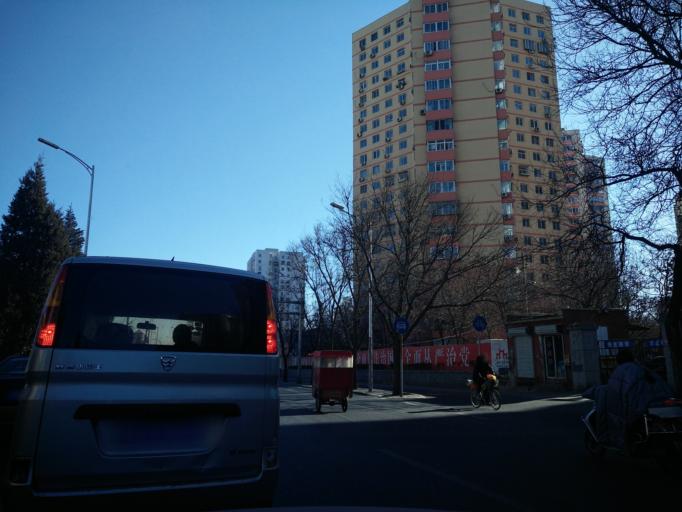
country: CN
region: Beijing
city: Dahongmen
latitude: 39.8555
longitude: 116.4061
